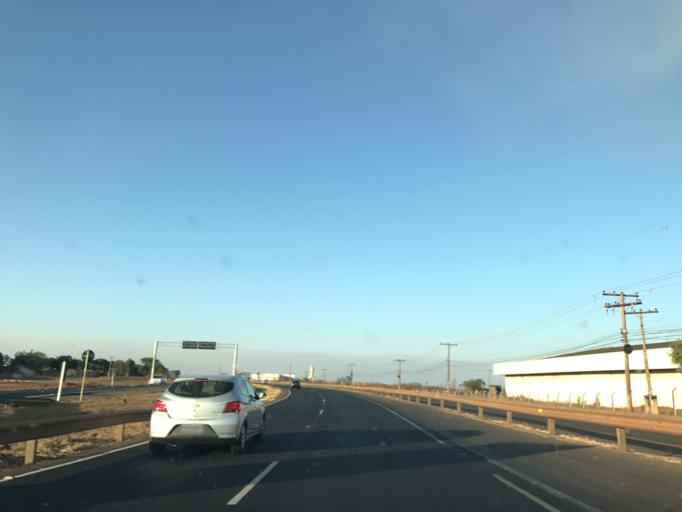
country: BR
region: Goias
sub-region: Anapolis
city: Anapolis
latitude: -16.3935
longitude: -48.9597
